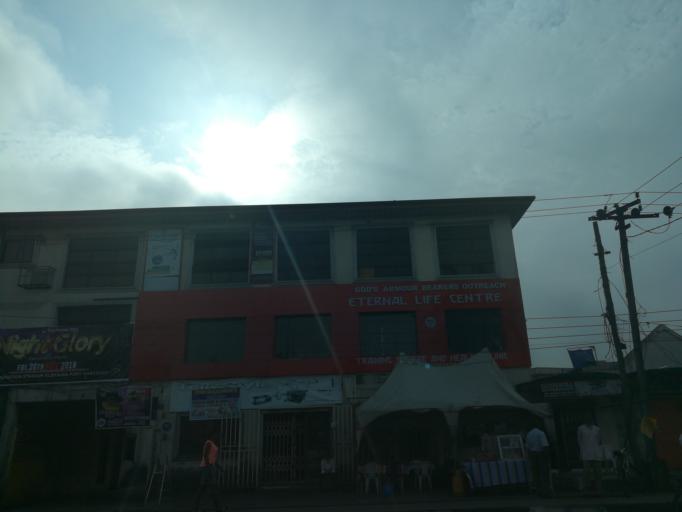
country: NG
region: Rivers
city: Port Harcourt
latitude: 4.8061
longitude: 6.9988
